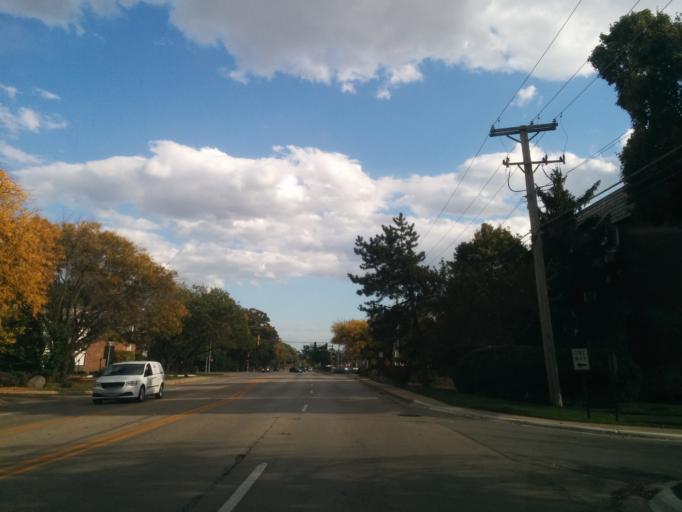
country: US
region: Illinois
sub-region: Cook County
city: Park Ridge
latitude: 42.0068
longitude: -87.8569
